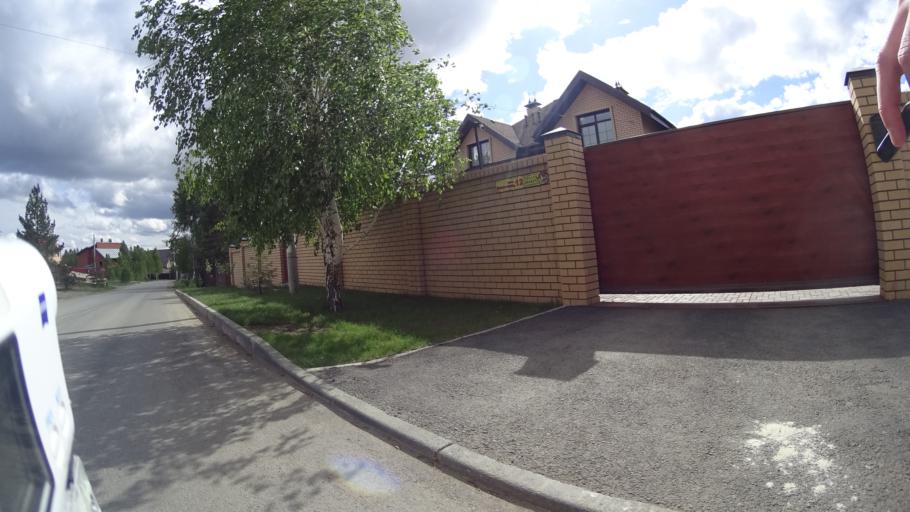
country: RU
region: Chelyabinsk
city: Sargazy
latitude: 55.1596
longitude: 61.2431
